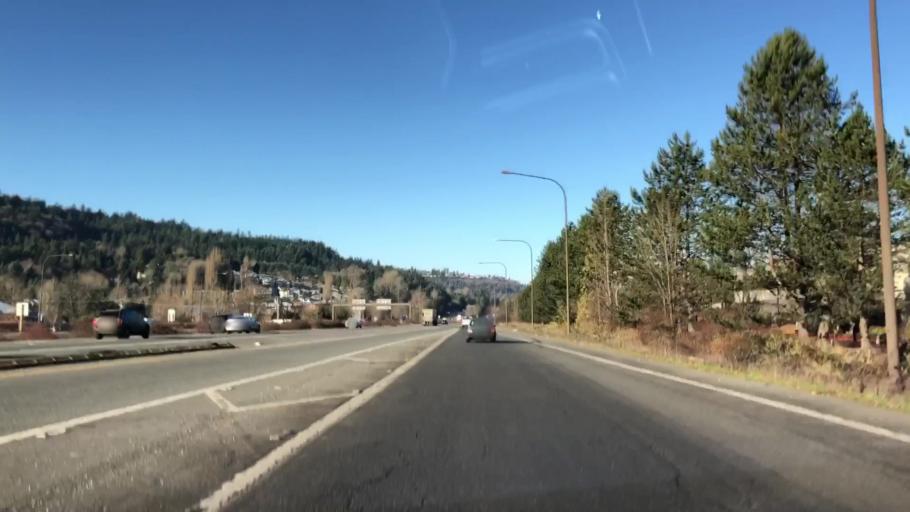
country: US
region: Washington
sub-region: King County
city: Issaquah
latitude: 47.5497
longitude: -122.0633
